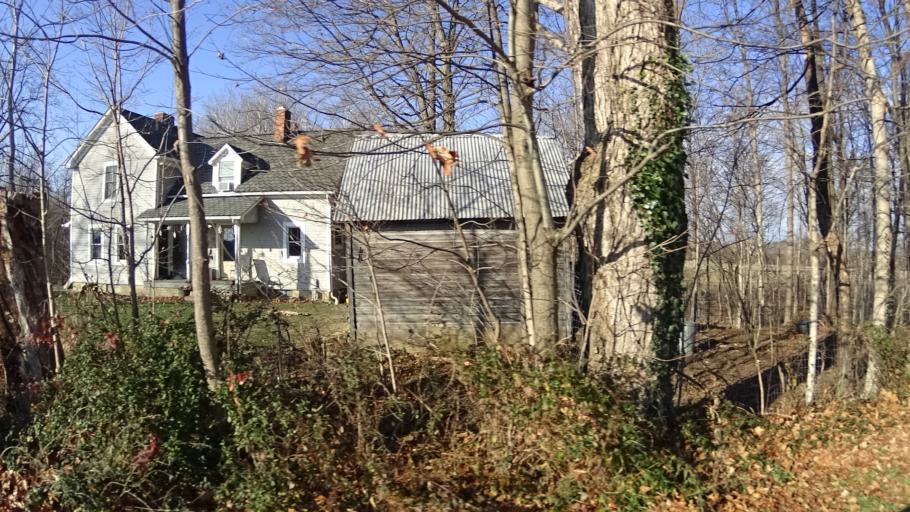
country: US
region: Ohio
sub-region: Lorain County
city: Oberlin
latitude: 41.2639
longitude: -82.1795
